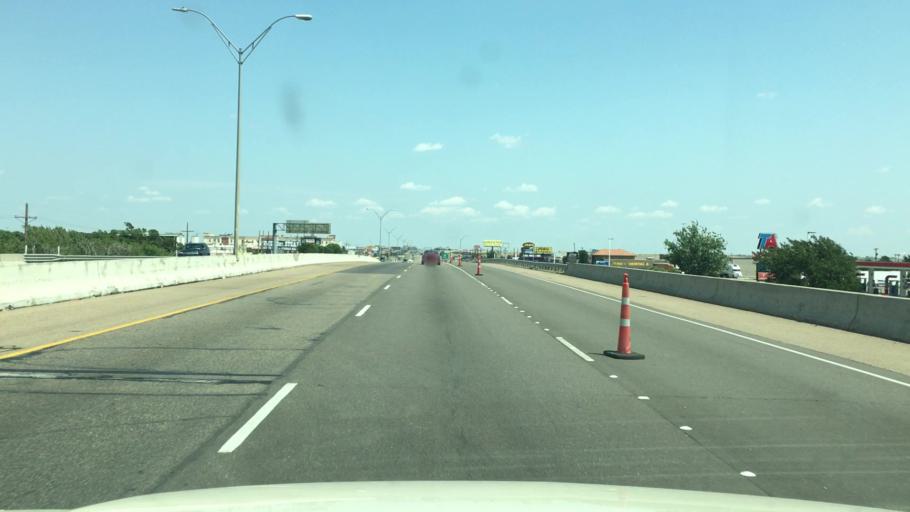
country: US
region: Texas
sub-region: Potter County
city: Amarillo
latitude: 35.1926
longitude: -101.7603
